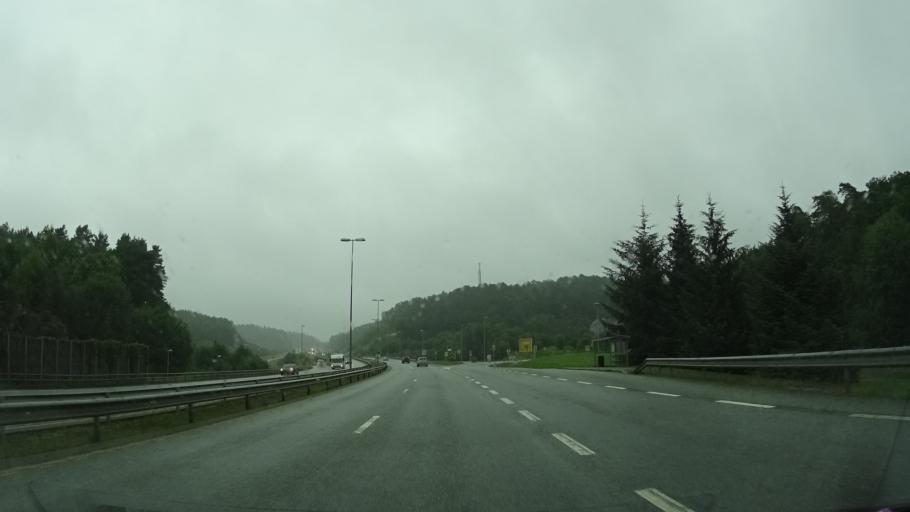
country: NO
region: Vest-Agder
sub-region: Kristiansand
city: Tveit
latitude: 58.1687
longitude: 8.1049
